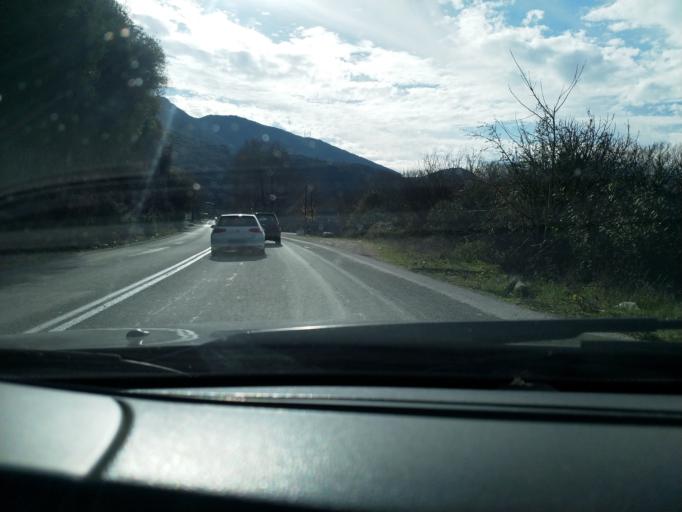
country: GR
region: Epirus
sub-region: Nomos Ioanninon
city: Agia Kyriaki
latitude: 39.4333
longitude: 20.8455
